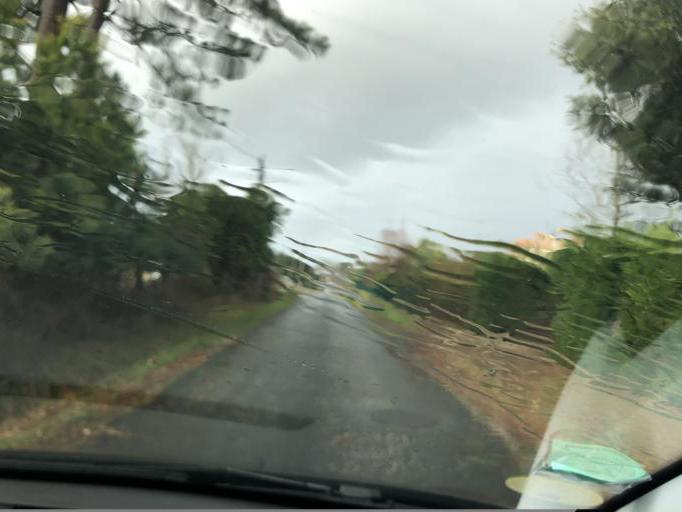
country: FR
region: Aquitaine
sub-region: Departement de la Gironde
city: Hourtin
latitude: 45.1778
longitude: -1.0512
